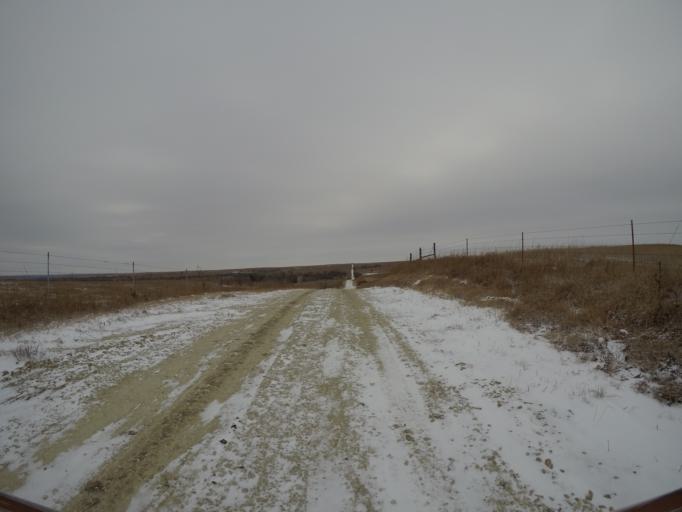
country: US
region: Kansas
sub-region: Wabaunsee County
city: Alma
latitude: 38.8708
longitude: -96.1135
